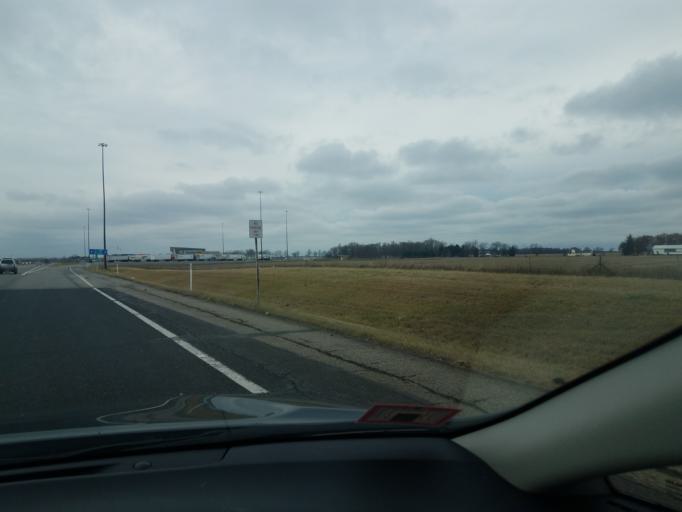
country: US
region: Michigan
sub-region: Saint Joseph County
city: Sturgis
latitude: 41.7449
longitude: -85.3241
